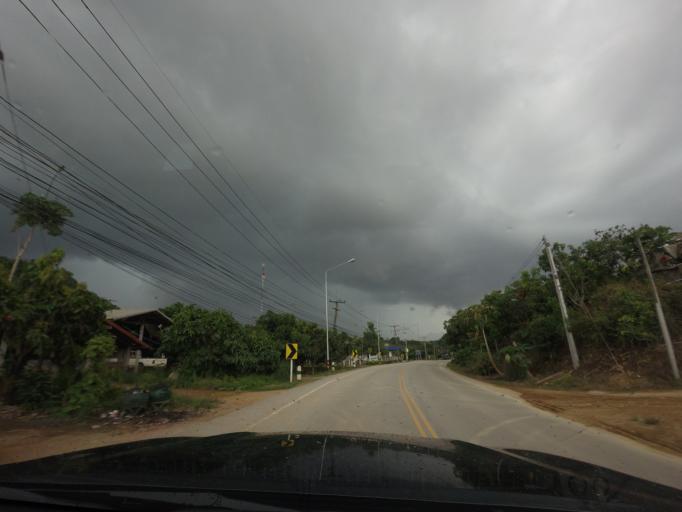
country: LA
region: Vientiane
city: Muang Sanakham
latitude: 17.9484
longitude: 101.7403
